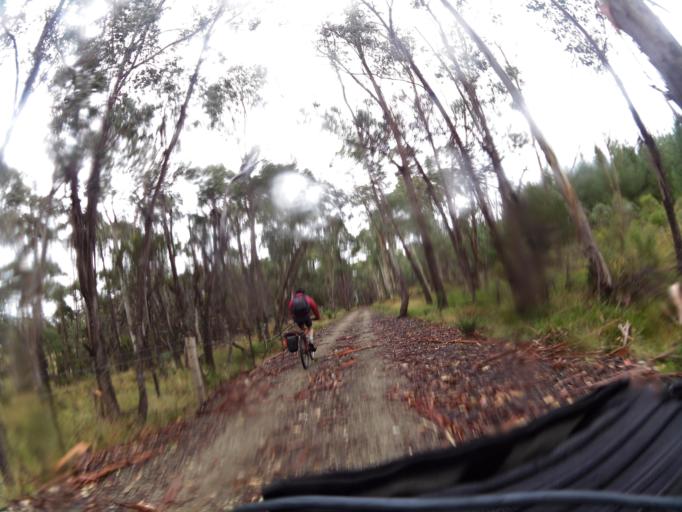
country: AU
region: New South Wales
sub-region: Greater Hume Shire
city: Holbrook
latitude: -36.1770
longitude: 147.5005
